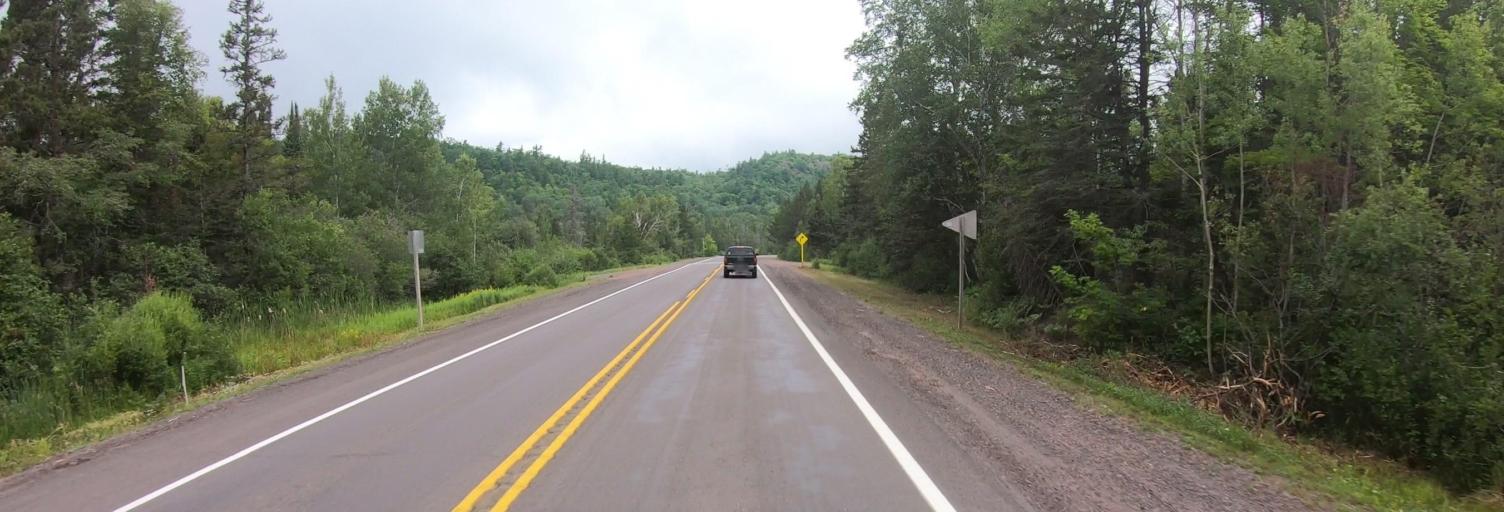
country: US
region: Michigan
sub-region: Keweenaw County
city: Eagle River
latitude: 47.3736
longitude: -88.3044
